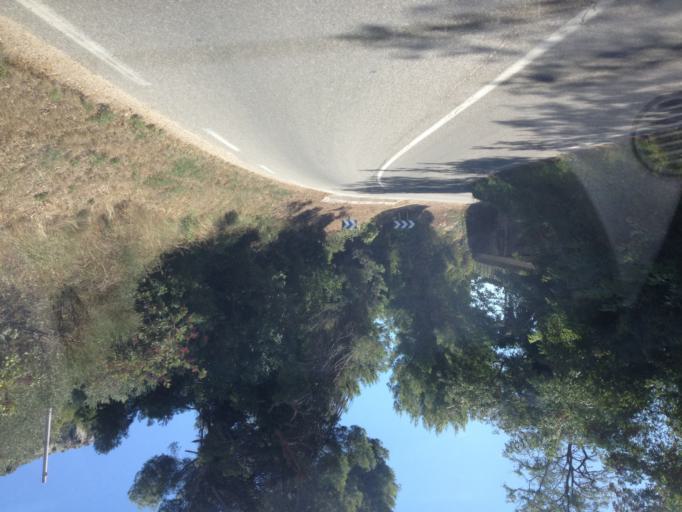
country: FR
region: Languedoc-Roussillon
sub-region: Departement du Gard
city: Villeneuve-les-Avignon
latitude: 43.9911
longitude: 4.8091
